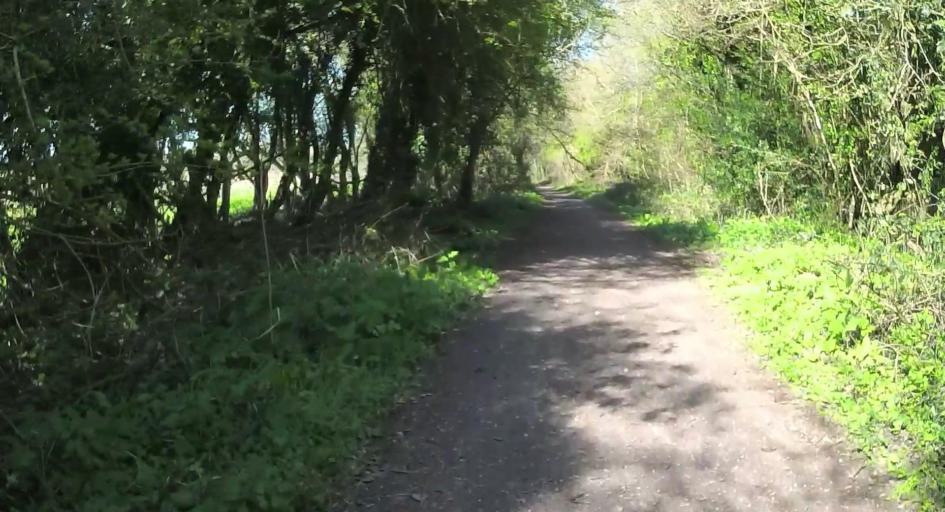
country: GB
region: England
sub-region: Hampshire
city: Romsey
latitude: 51.0919
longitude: -1.4985
